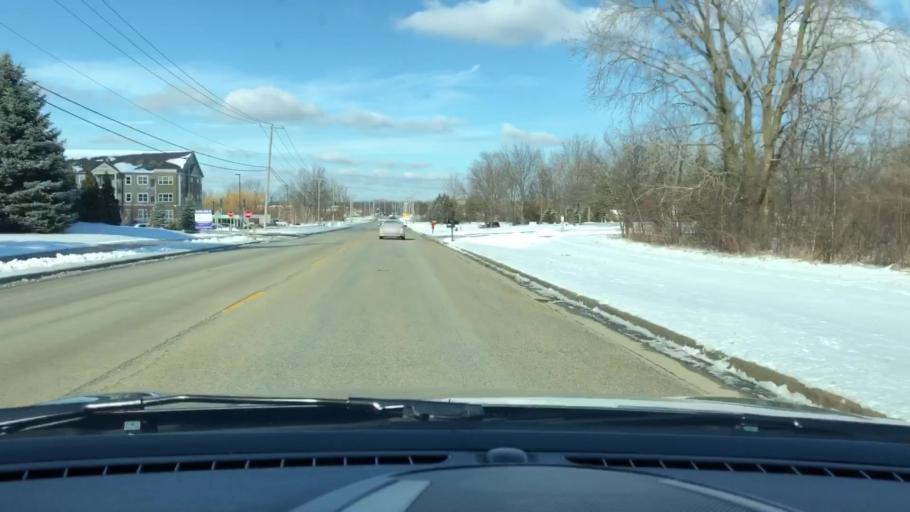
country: US
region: Illinois
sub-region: Will County
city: Mokena
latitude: 41.4955
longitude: -87.8882
